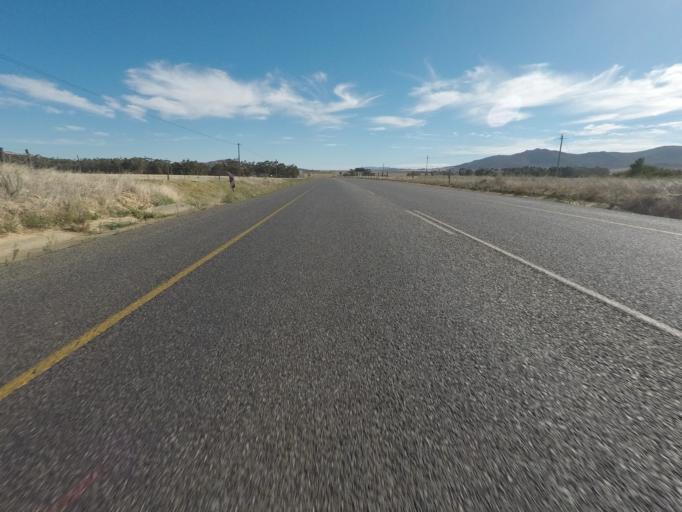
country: ZA
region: Western Cape
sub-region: West Coast District Municipality
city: Malmesbury
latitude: -33.6207
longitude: 18.7259
